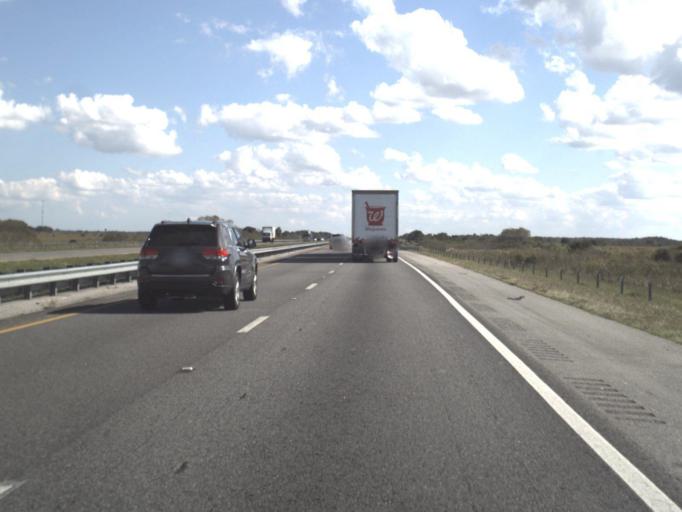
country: US
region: Florida
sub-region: Indian River County
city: Fellsmere
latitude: 27.8010
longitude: -80.9940
